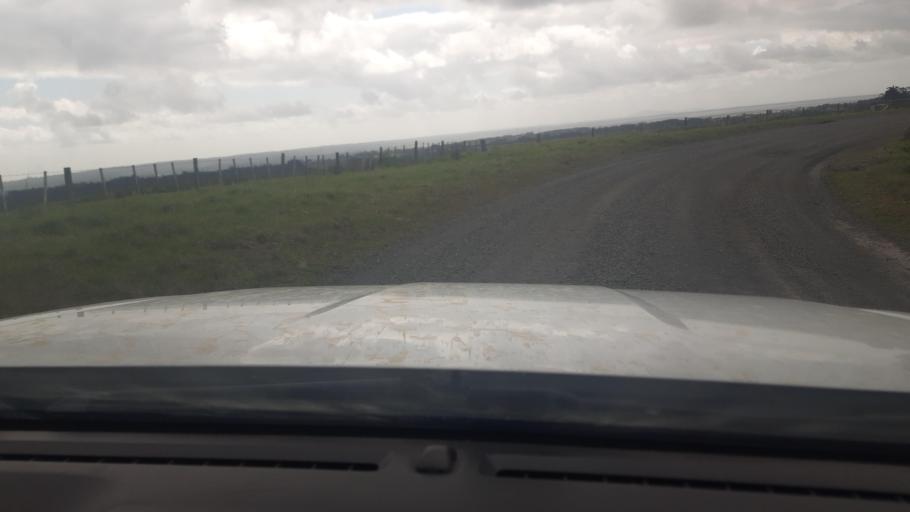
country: NZ
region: Northland
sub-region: Far North District
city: Kaitaia
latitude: -35.0626
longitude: 173.3224
